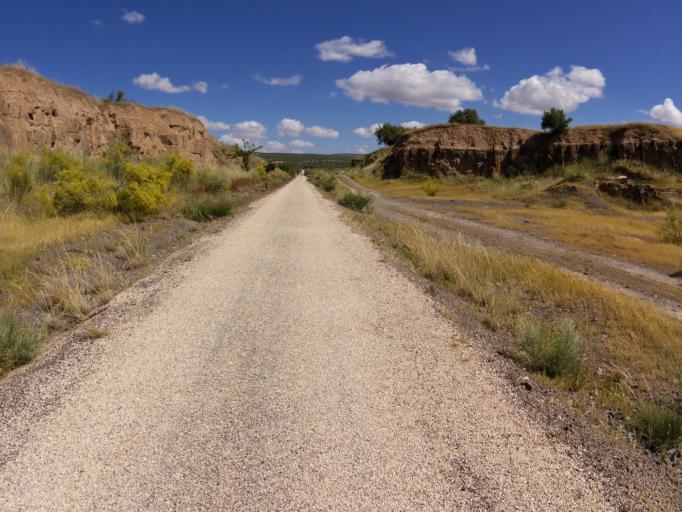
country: ES
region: Andalusia
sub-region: Provincia de Jaen
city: Alcaudete
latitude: 37.6345
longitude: -4.0825
